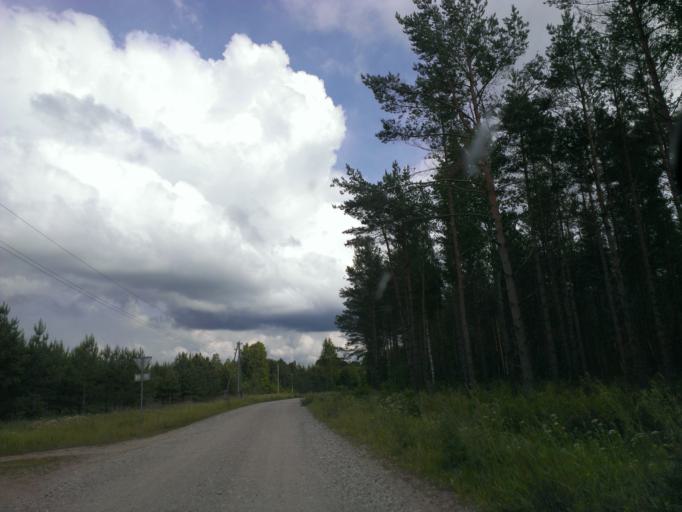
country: LT
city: Skuodas
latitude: 56.3269
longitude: 21.3177
